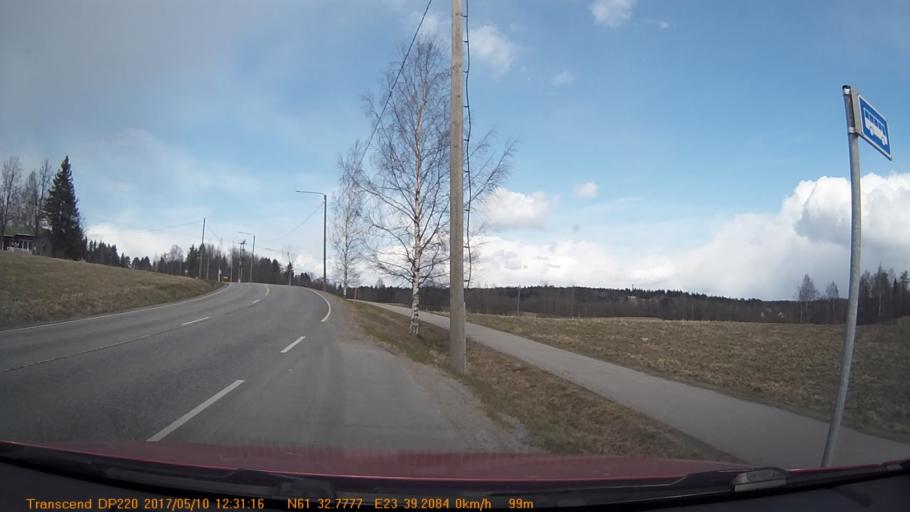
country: FI
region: Pirkanmaa
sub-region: Tampere
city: Yloejaervi
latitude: 61.5463
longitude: 23.6535
